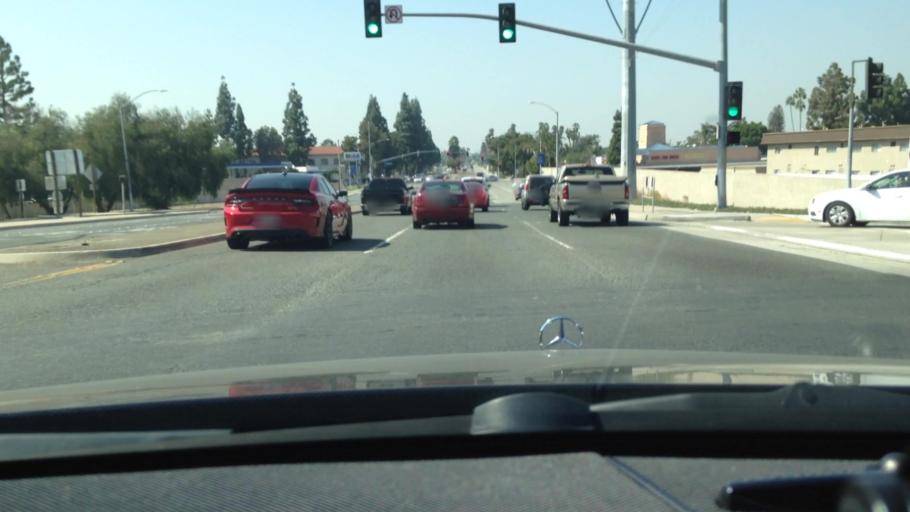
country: US
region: California
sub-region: Orange County
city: Placentia
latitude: 33.8382
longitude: -117.8780
